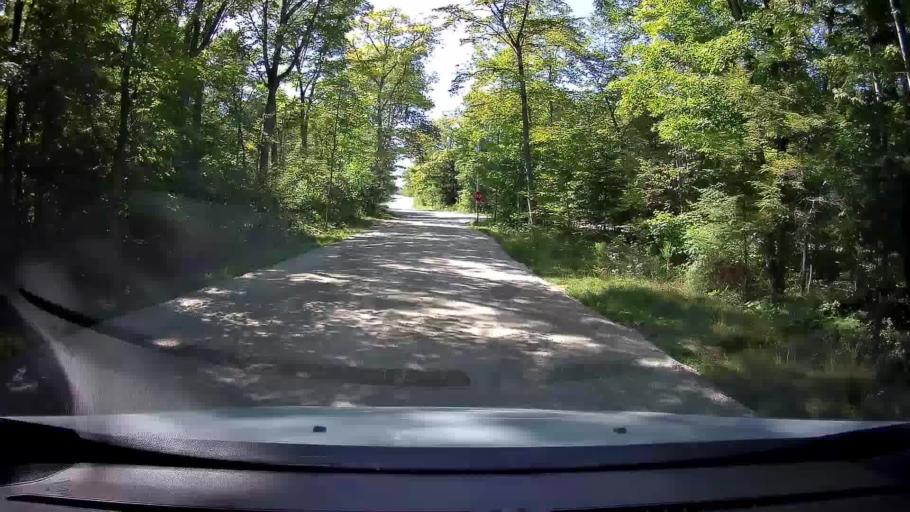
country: US
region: Michigan
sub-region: Delta County
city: Escanaba
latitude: 45.2893
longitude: -86.9792
